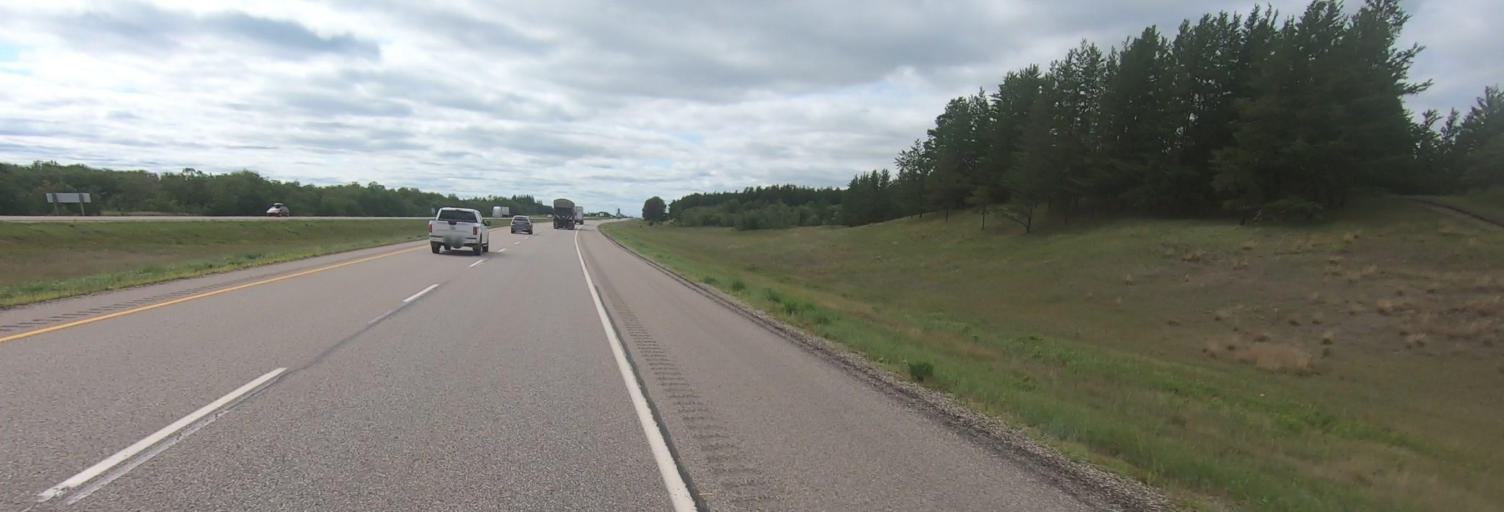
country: CA
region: Manitoba
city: Carberry
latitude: 49.9023
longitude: -99.5655
